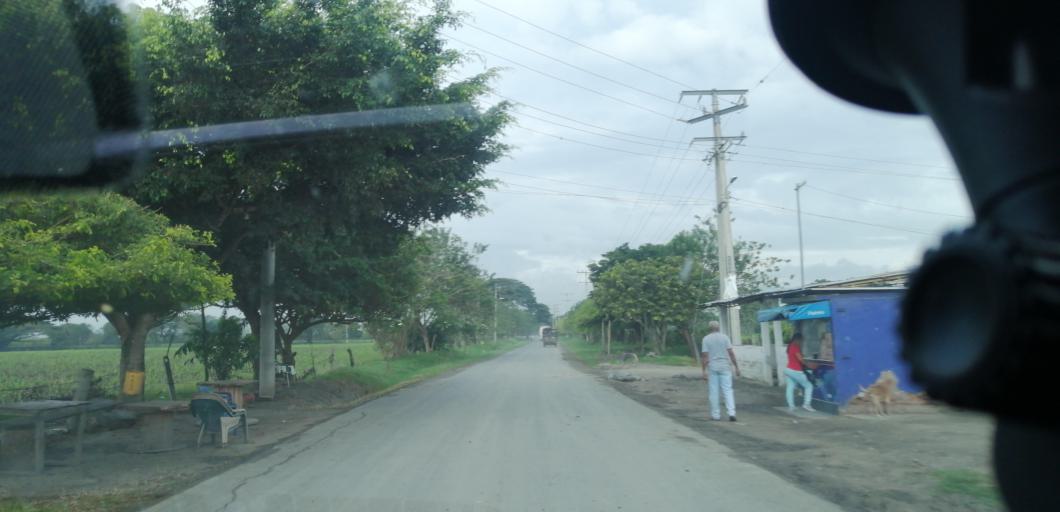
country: CO
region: Valle del Cauca
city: Yumbo
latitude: 3.5745
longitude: -76.4055
